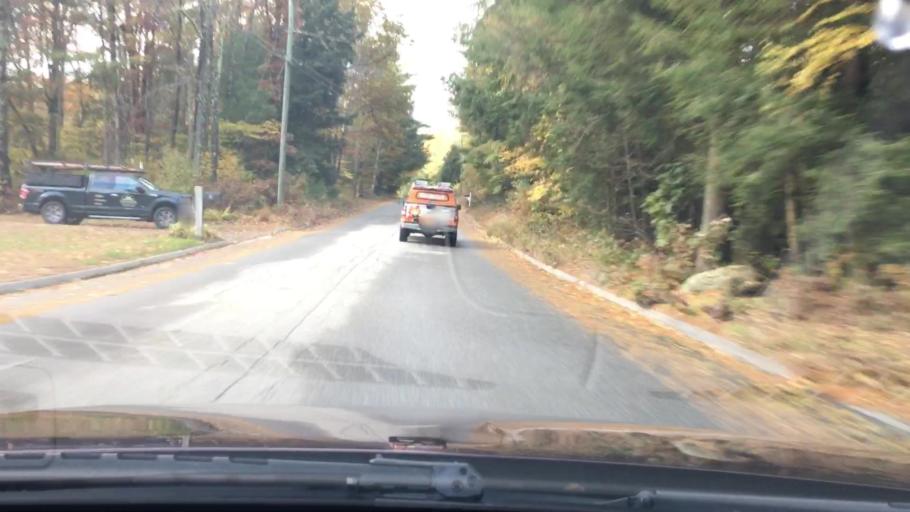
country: US
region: Connecticut
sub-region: Tolland County
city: Stafford Springs
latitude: 41.9796
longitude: -72.3278
